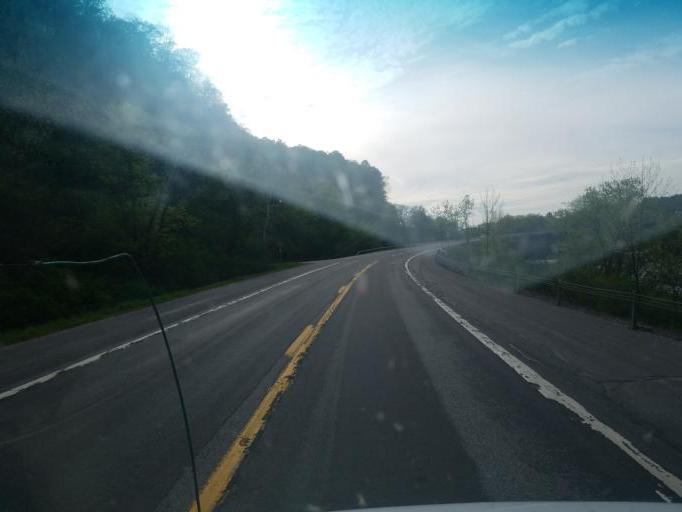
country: US
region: New York
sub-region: Herkimer County
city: Little Falls
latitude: 43.0363
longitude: -74.8415
